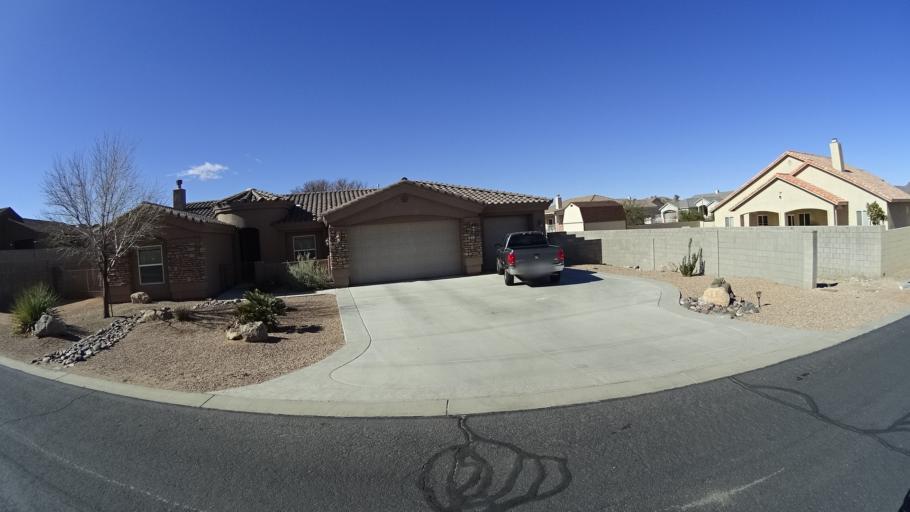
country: US
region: Arizona
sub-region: Mohave County
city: Kingman
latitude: 35.1888
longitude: -114.0252
